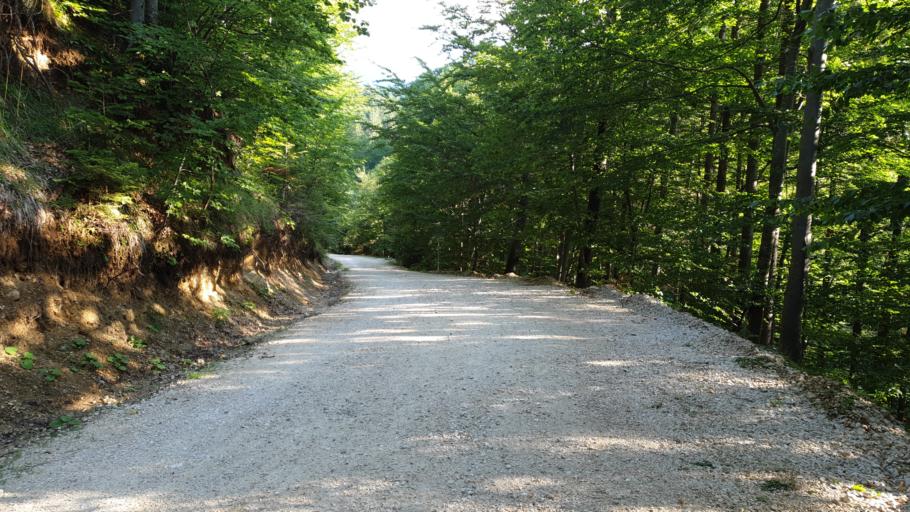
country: RO
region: Brasov
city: Brasov
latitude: 45.6131
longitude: 25.5572
